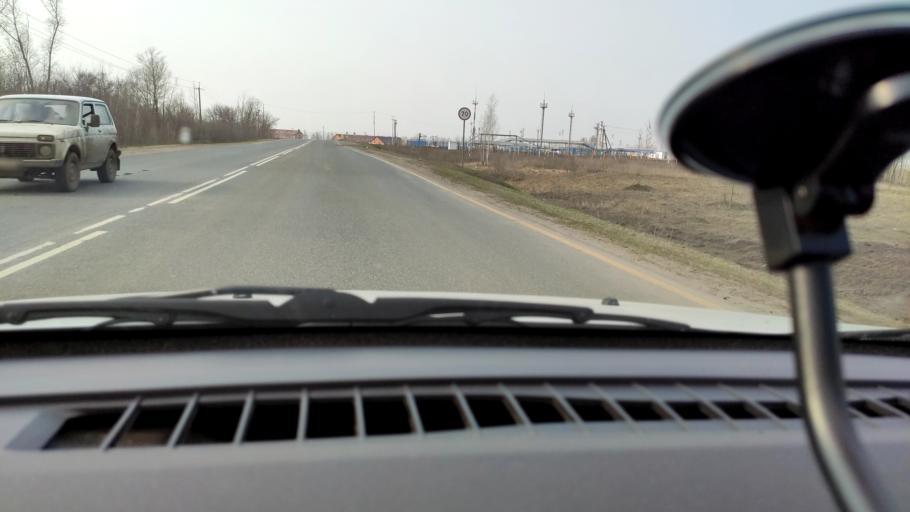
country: RU
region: Samara
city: Dubovyy Umet
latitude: 53.0796
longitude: 50.3495
